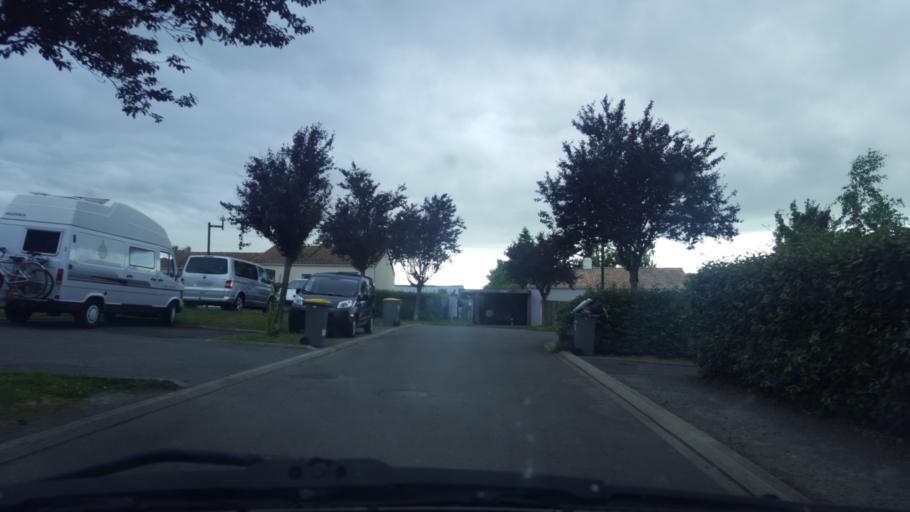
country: FR
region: Pays de la Loire
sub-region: Departement de la Loire-Atlantique
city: Saint-Philbert-de-Grand-Lieu
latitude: 47.0328
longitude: -1.6406
